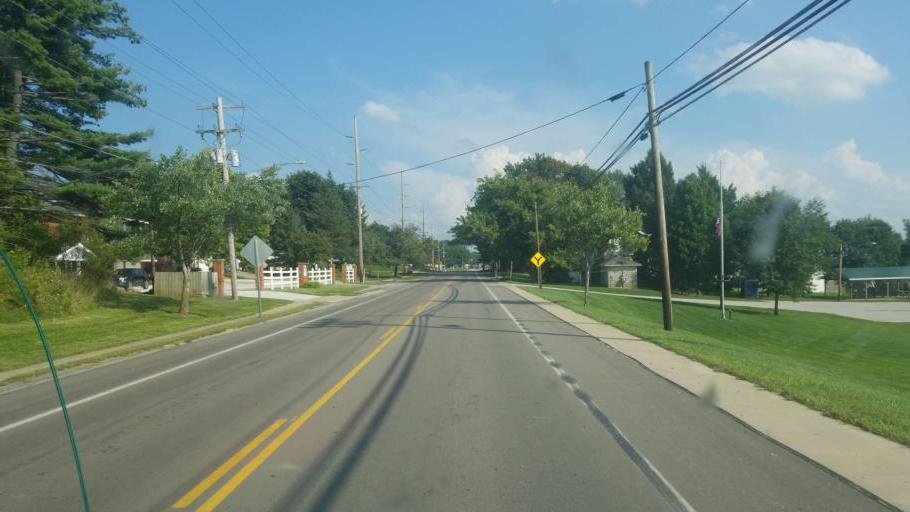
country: US
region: Ohio
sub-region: Medina County
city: Lodi
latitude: 41.0283
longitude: -82.0019
